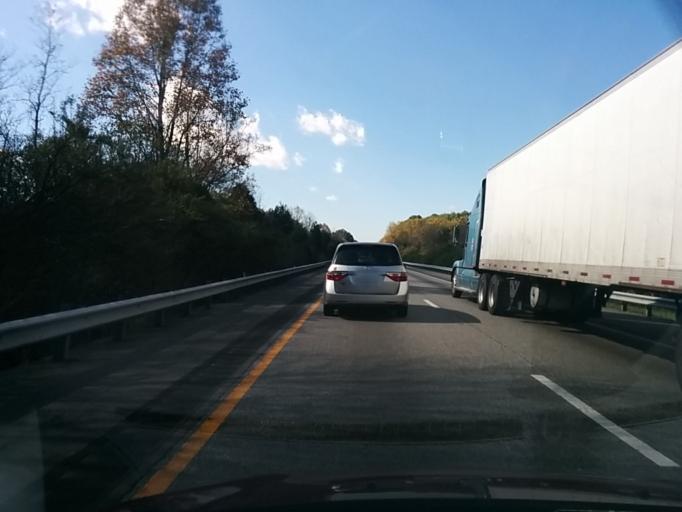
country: US
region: Virginia
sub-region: Botetourt County
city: Fincastle
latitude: 37.4521
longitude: -79.8499
